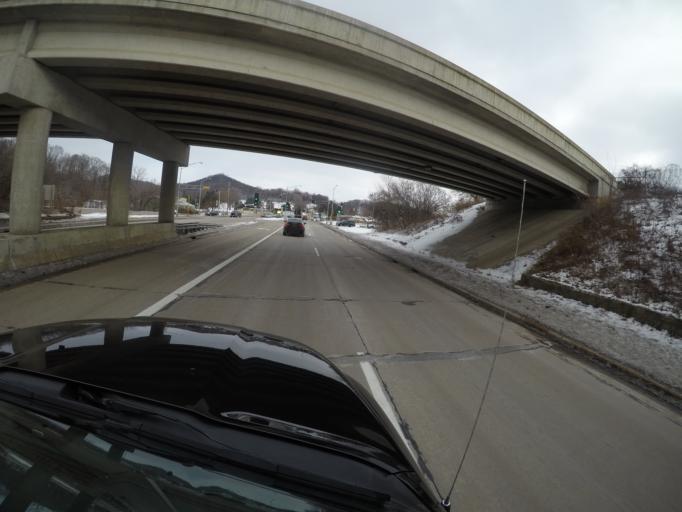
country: US
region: Wisconsin
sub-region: La Crosse County
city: Onalaska
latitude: 43.8842
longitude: -91.2115
